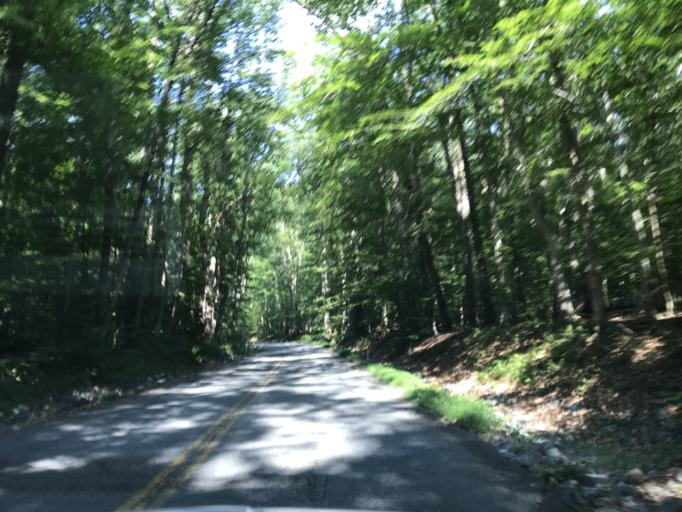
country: US
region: Maryland
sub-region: Harford County
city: South Bel Air
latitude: 39.6180
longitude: -76.2827
